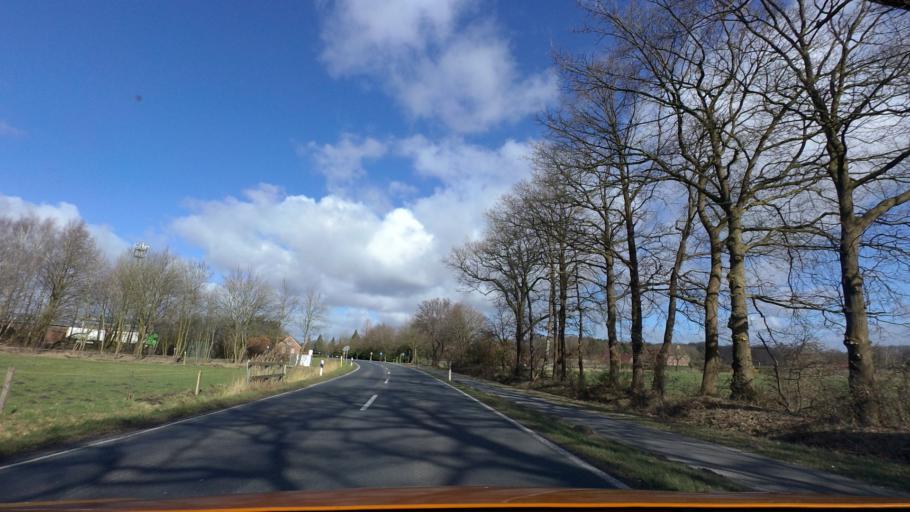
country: DE
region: Lower Saxony
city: Edewecht
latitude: 53.1504
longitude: 7.9995
